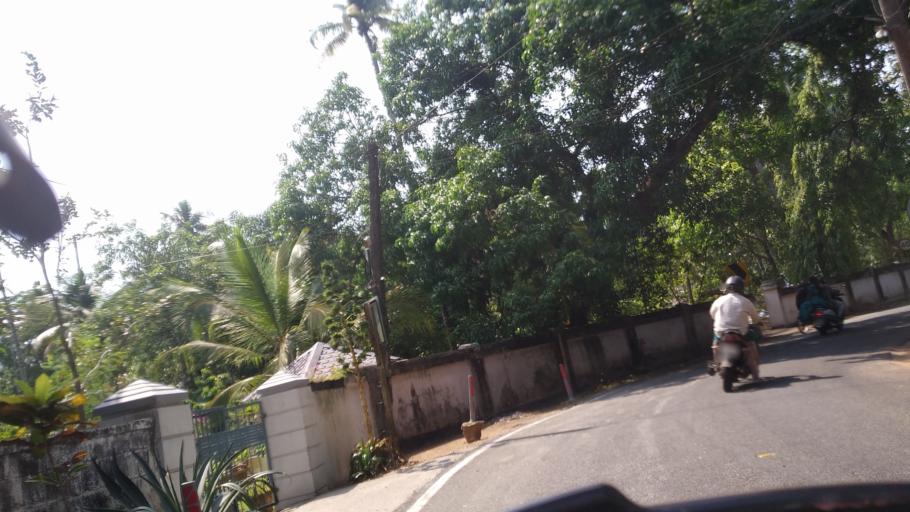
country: IN
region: Kerala
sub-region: Thrissur District
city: Irinjalakuda
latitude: 10.3008
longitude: 76.1314
